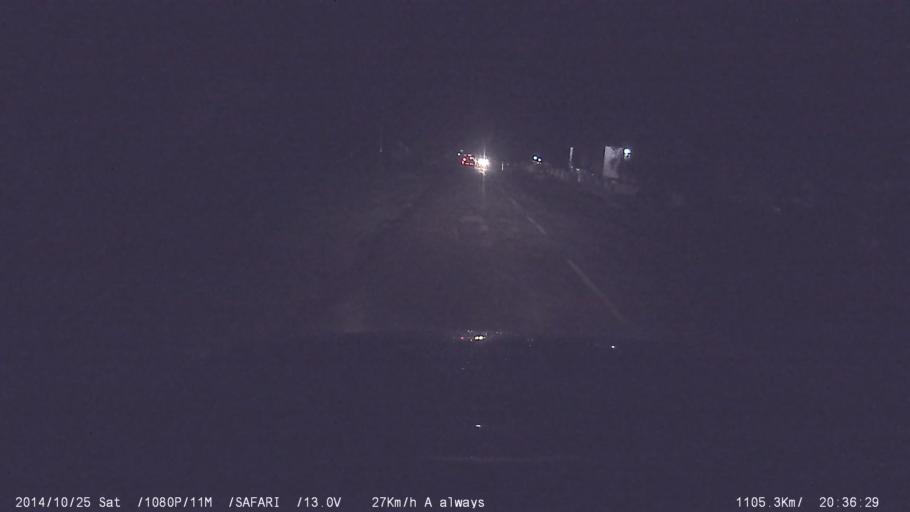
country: IN
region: Kerala
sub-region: Kottayam
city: Palackattumala
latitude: 9.6881
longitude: 76.5577
